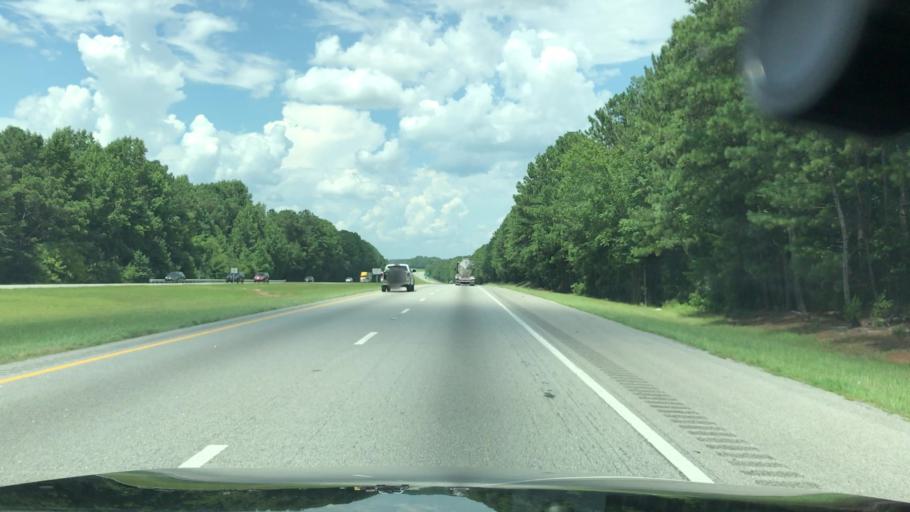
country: US
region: South Carolina
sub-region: Chester County
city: Eureka Mill
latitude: 34.6969
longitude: -81.0295
